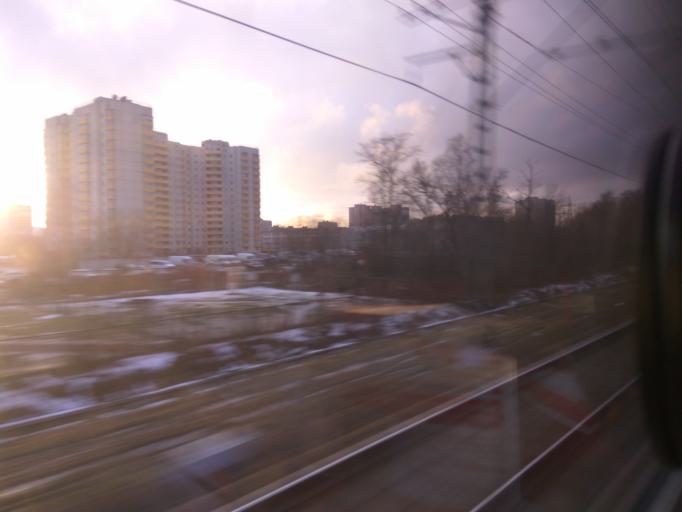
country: RU
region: St.-Petersburg
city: Obukhovo
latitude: 59.8732
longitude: 30.4155
